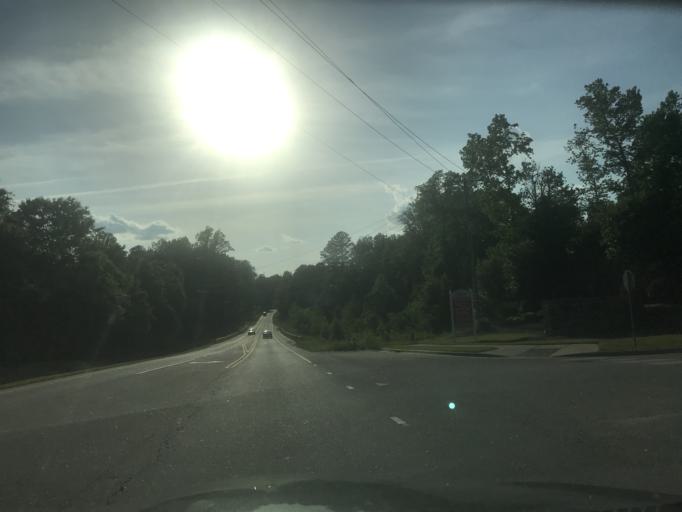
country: US
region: North Carolina
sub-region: Wake County
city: Knightdale
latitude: 35.7540
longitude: -78.5070
